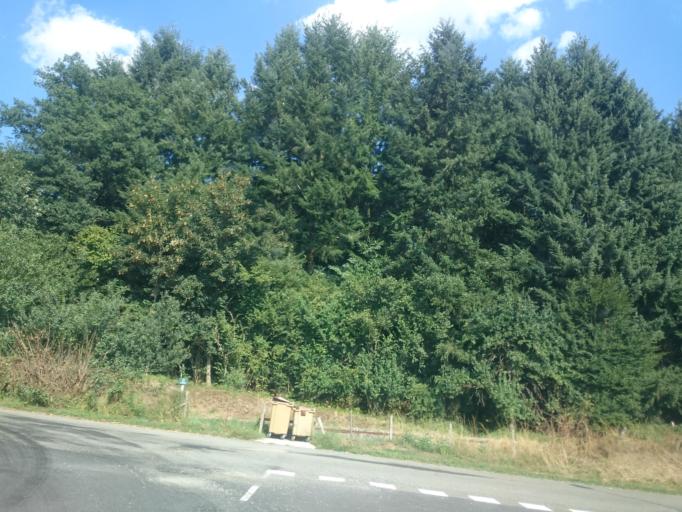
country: FR
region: Auvergne
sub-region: Departement du Cantal
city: Saint-Mamet-la-Salvetat
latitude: 44.8534
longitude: 2.2340
